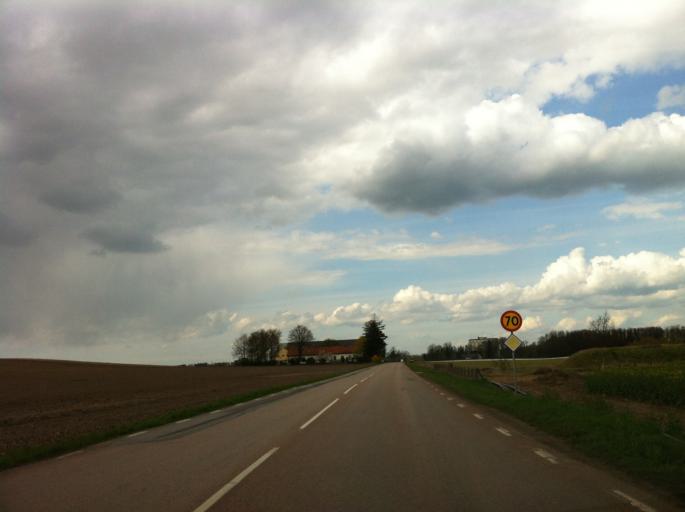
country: SE
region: Skane
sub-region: Svalovs Kommun
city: Teckomatorp
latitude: 55.8423
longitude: 13.1033
